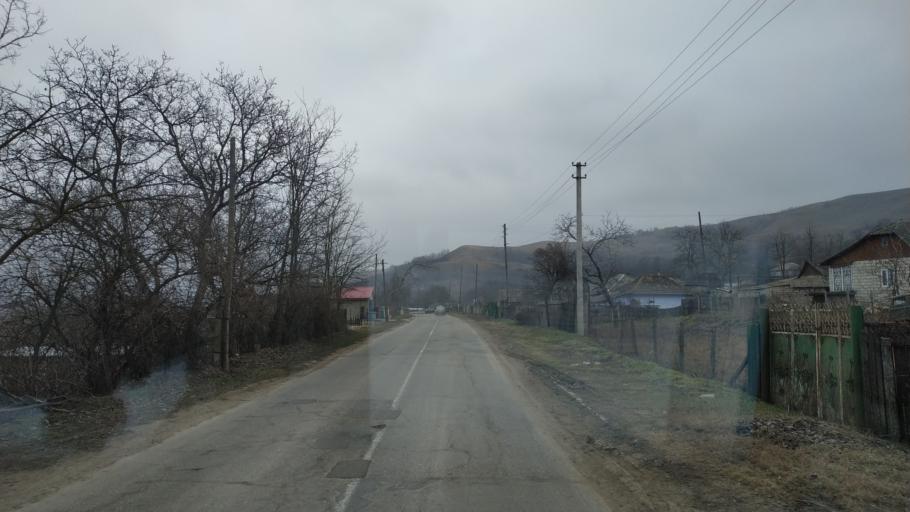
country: MD
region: Hincesti
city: Hincesti
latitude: 46.9813
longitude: 28.4525
